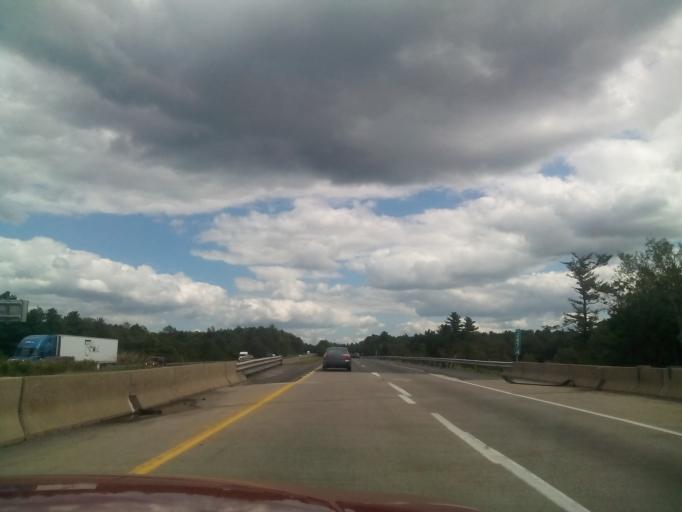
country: US
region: Pennsylvania
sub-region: Monroe County
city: Pocono Pines
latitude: 41.0765
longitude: -75.5061
